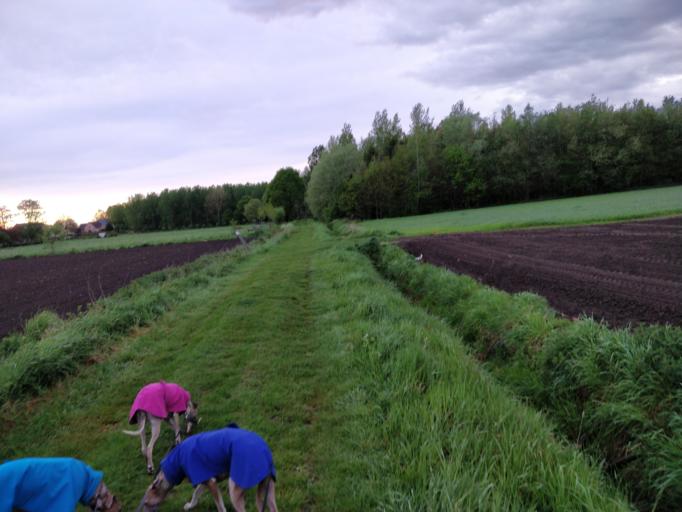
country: BE
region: Flanders
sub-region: Provincie Antwerpen
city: Mechelen
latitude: 51.0258
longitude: 4.4286
